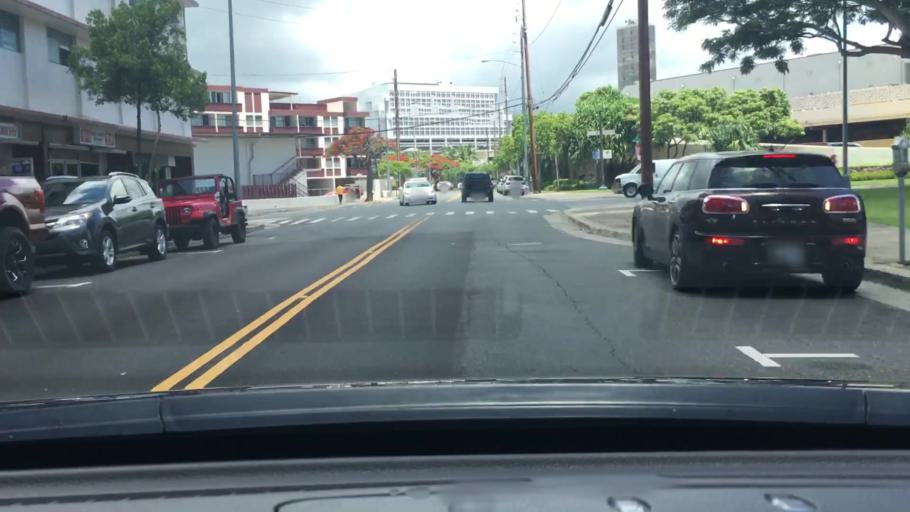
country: US
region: Hawaii
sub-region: Honolulu County
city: Honolulu
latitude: 21.2949
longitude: -157.8449
